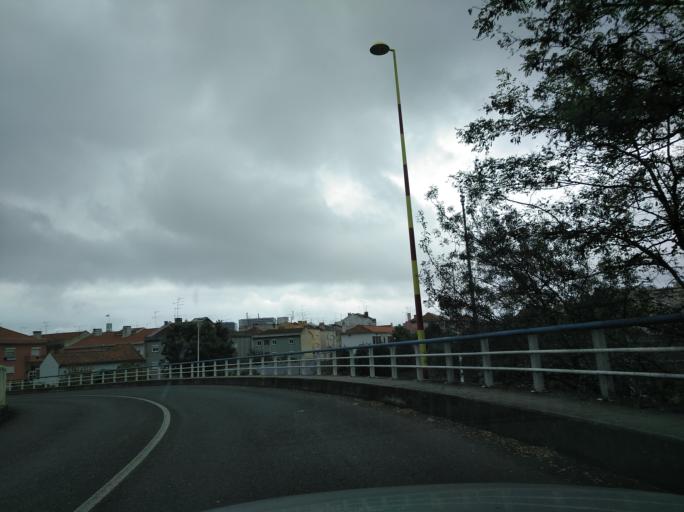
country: PT
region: Lisbon
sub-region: Loures
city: Moscavide
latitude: 38.7791
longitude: -9.1058
